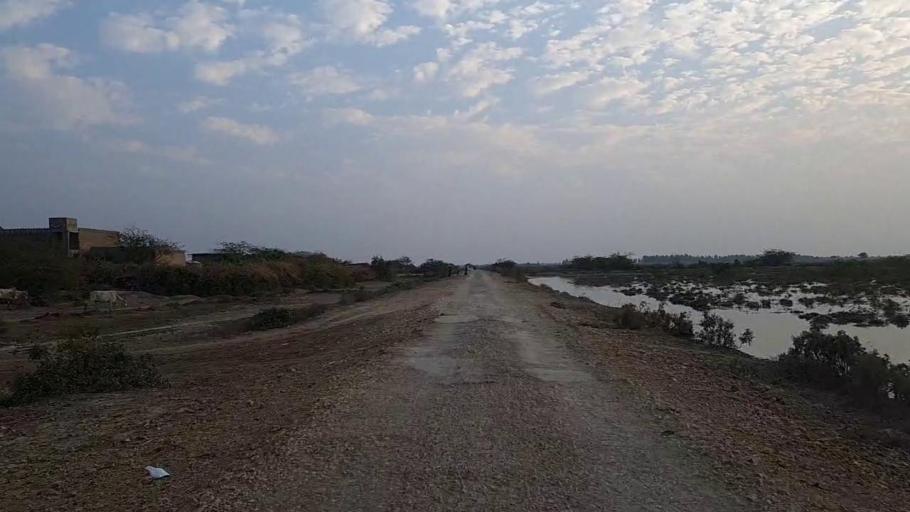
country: PK
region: Sindh
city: Pithoro
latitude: 25.4533
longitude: 69.3452
